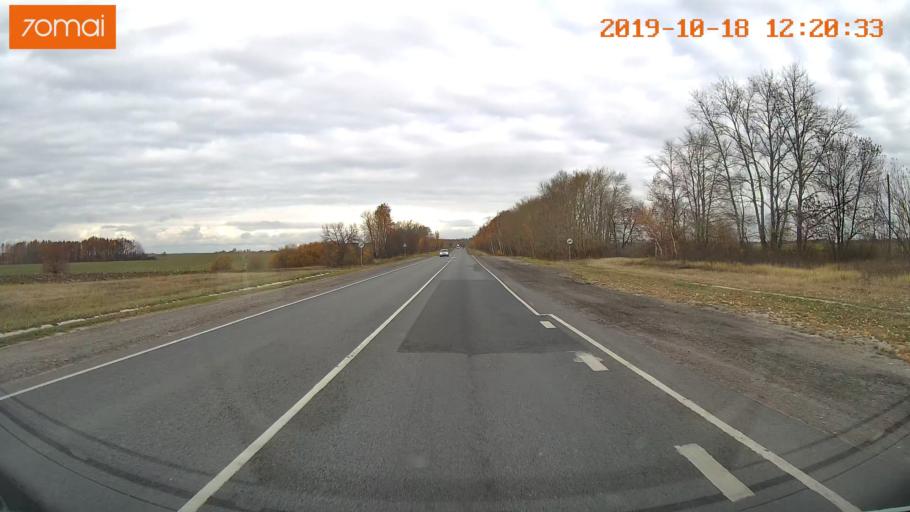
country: RU
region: Rjazan
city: Bagramovo
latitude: 54.4995
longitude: 39.4817
